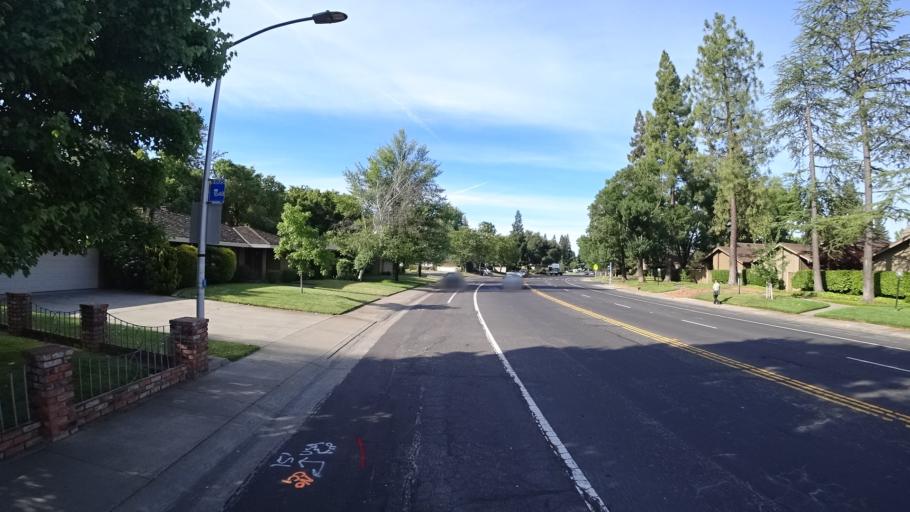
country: US
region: California
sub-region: Sacramento County
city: Arden-Arcade
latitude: 38.5713
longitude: -121.4015
